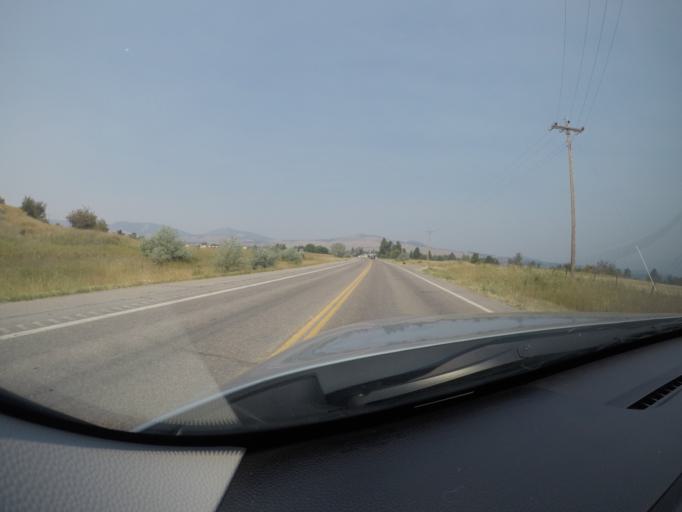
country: US
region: Montana
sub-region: Lake County
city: Polson
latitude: 47.7080
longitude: -114.1850
